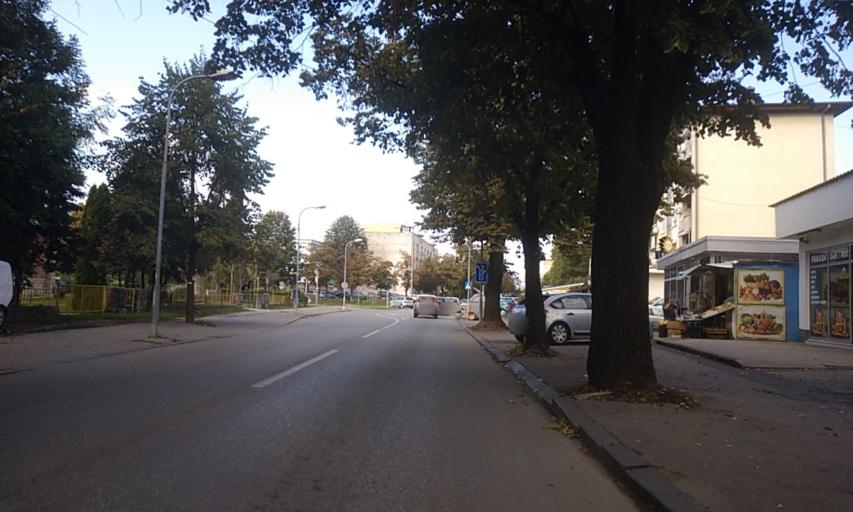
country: BA
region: Republika Srpska
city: Hiseti
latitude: 44.7642
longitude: 17.1838
